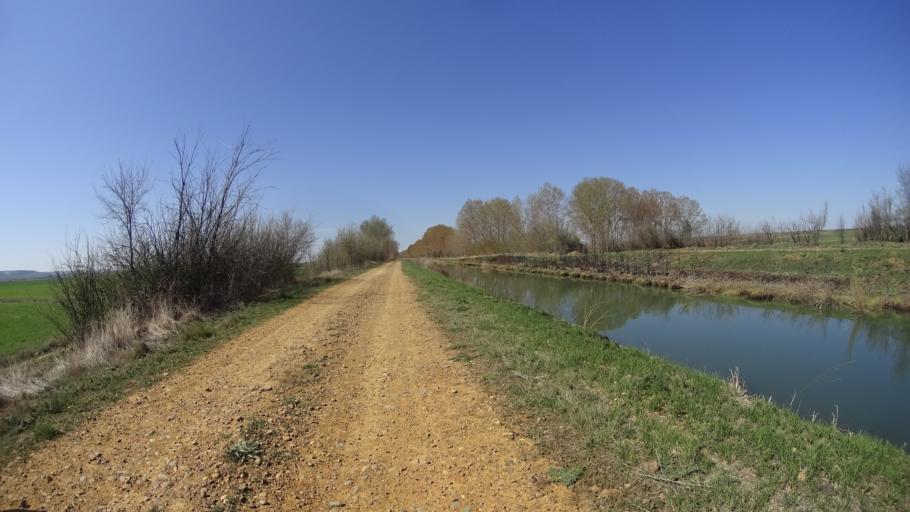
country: ES
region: Castille and Leon
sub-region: Provincia de Palencia
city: Pina de Campos
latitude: 42.2114
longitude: -4.4579
